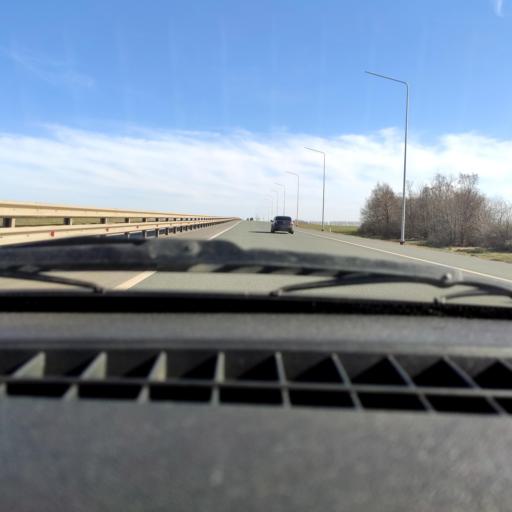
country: RU
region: Bashkortostan
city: Tolbazy
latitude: 54.1773
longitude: 55.8989
